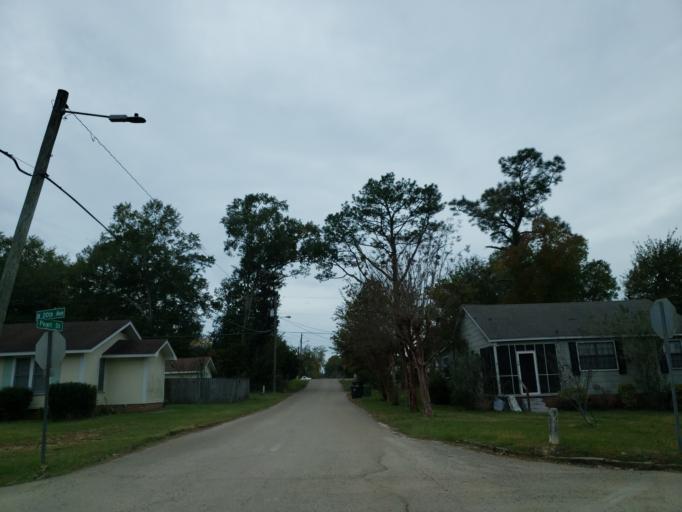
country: US
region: Mississippi
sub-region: Forrest County
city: Hattiesburg
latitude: 31.3266
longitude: -89.3216
